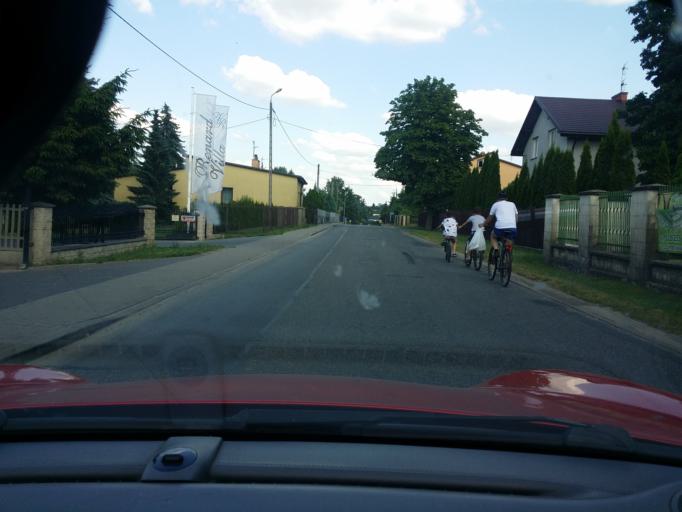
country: PL
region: Masovian Voivodeship
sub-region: Powiat radomski
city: Trablice
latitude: 51.3522
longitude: 21.1313
